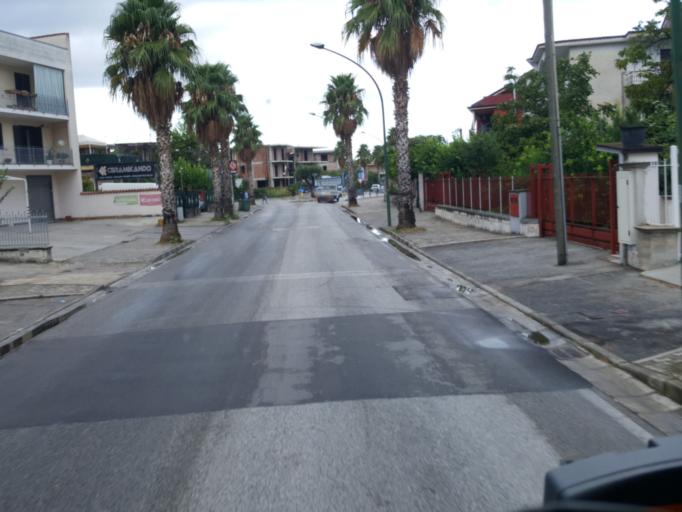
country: IT
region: Campania
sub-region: Provincia di Napoli
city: Palma Campania
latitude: 40.8595
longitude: 14.5499
